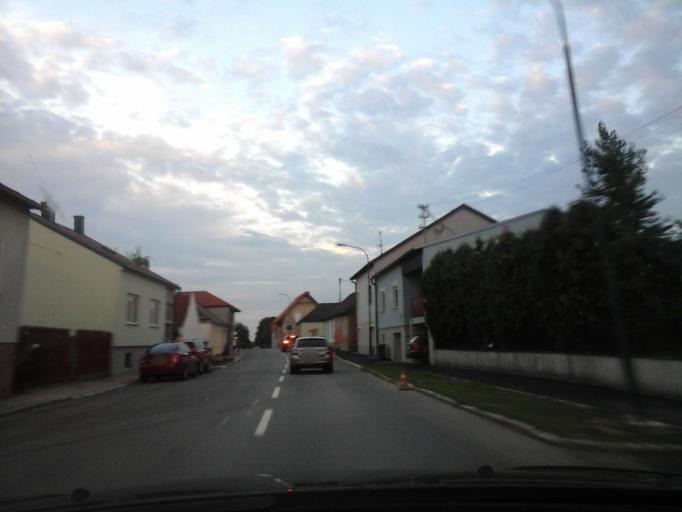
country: AT
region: Lower Austria
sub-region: Politischer Bezirk Bruck an der Leitha
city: Scharndorf
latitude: 48.0958
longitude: 16.7951
